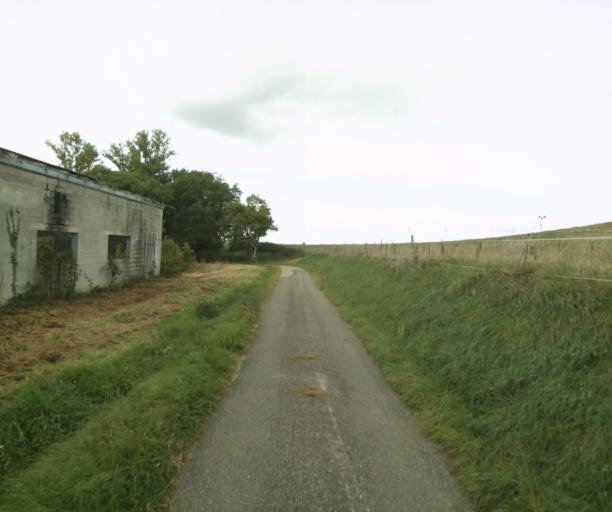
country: FR
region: Midi-Pyrenees
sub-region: Departement du Gers
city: Gondrin
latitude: 43.8641
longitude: 0.2306
